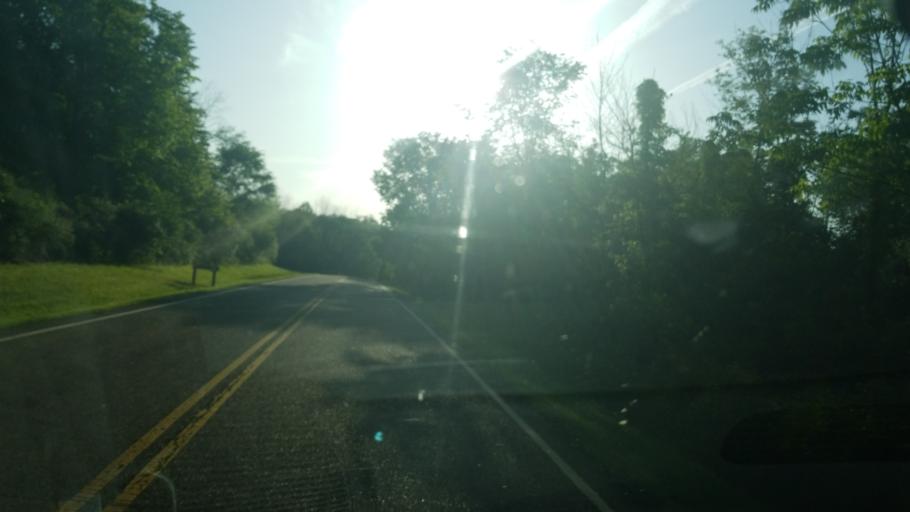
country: US
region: Ohio
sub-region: Portage County
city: Ravenna
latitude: 41.1314
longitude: -81.1445
